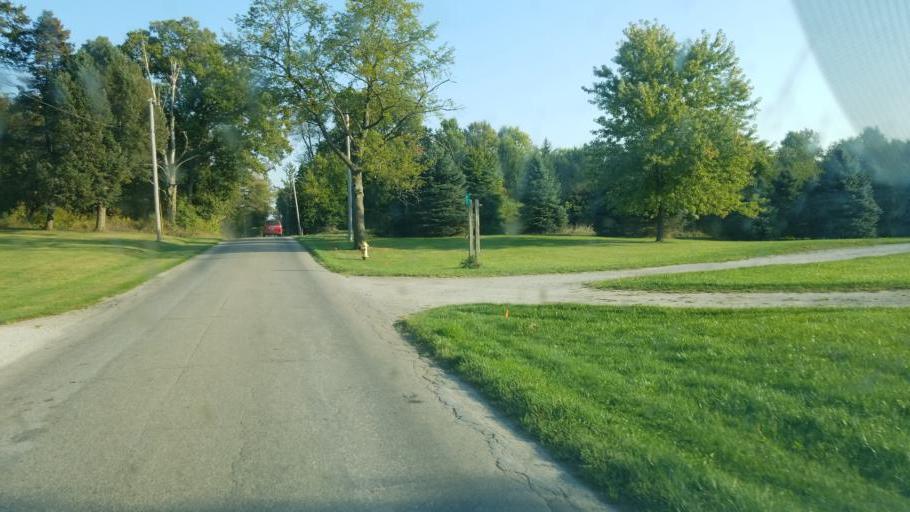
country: US
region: Indiana
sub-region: LaGrange County
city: Lagrange
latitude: 41.6364
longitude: -85.4247
